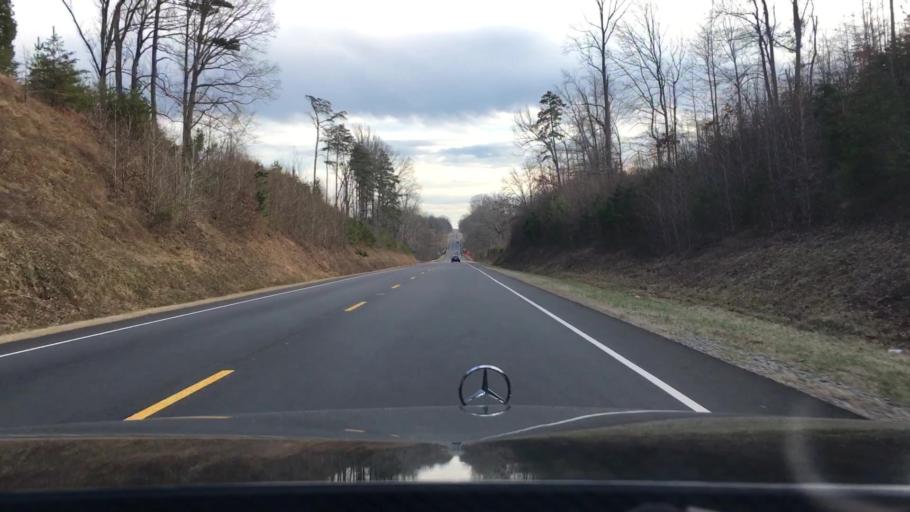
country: US
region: Virginia
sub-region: City of Danville
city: Danville
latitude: 36.5094
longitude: -79.3906
